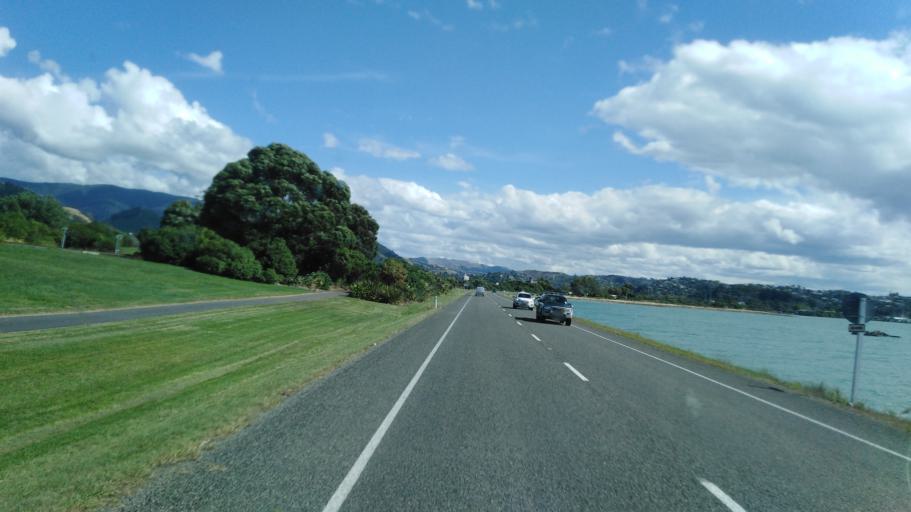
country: NZ
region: Nelson
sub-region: Nelson City
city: Nelson
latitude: -41.2599
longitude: 173.2953
